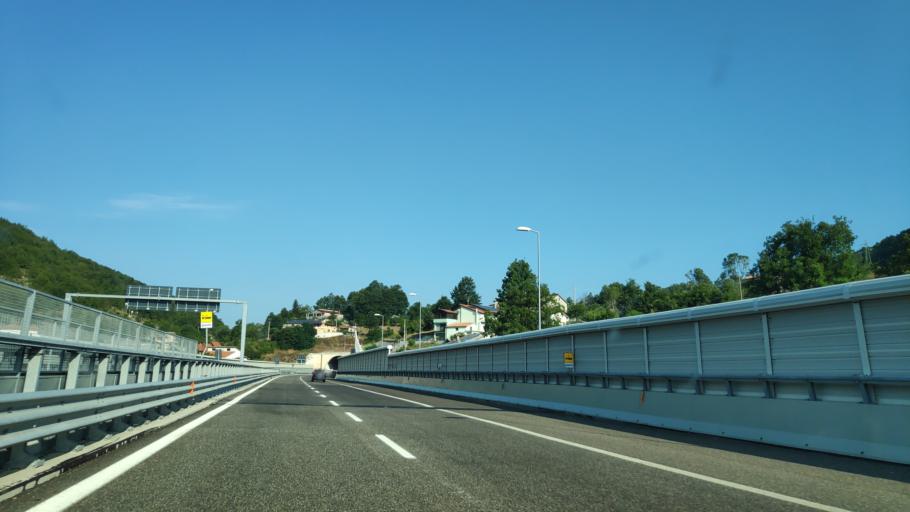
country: IT
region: Basilicate
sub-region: Provincia di Potenza
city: Lauria
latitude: 40.0200
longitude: 15.8835
